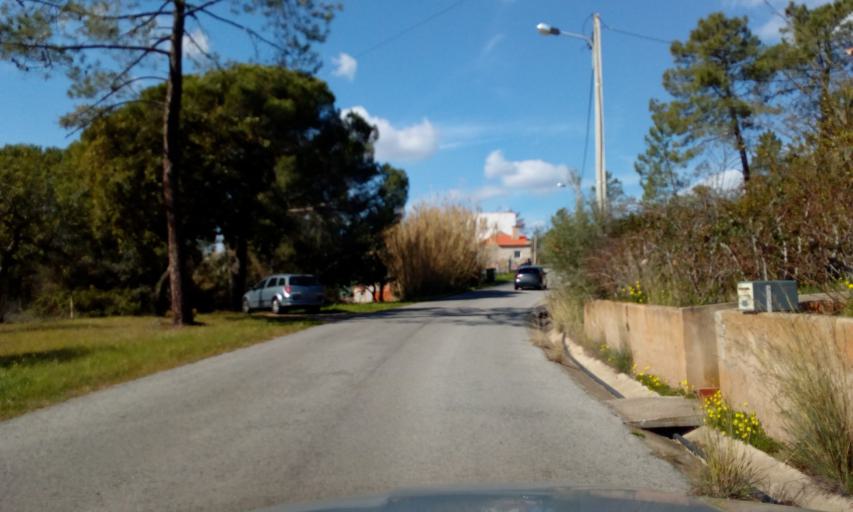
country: PT
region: Faro
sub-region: Loule
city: Loule
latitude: 37.2460
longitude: -8.0780
